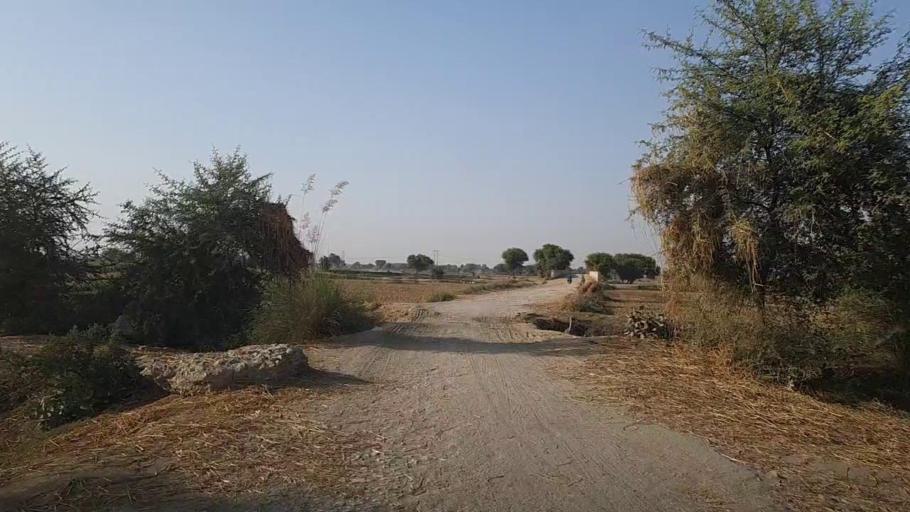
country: PK
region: Sindh
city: Kashmor
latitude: 28.4072
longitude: 69.4133
